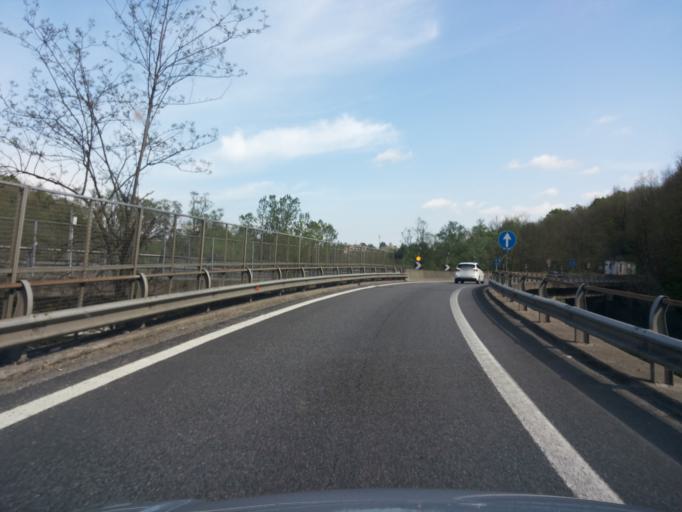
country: IT
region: Lombardy
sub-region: Provincia di Varese
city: Malnate
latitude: 45.8020
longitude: 8.8646
